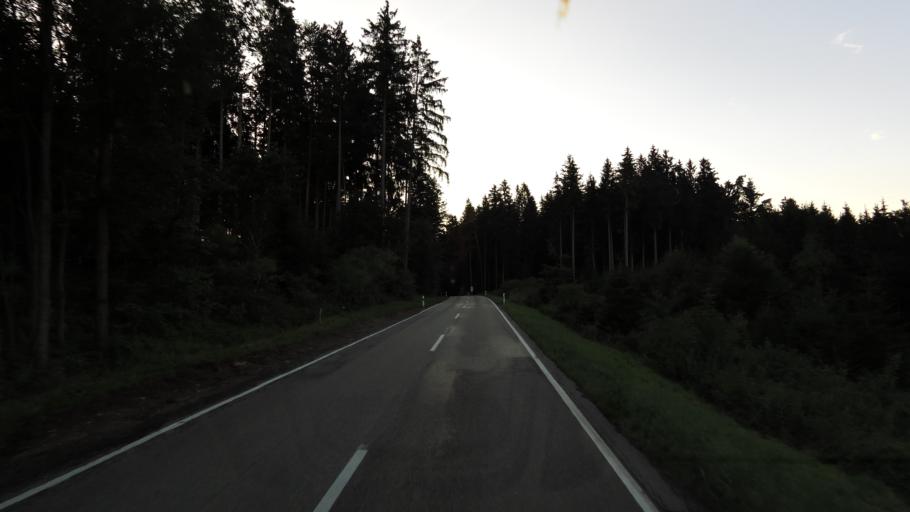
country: DE
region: Bavaria
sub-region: Upper Bavaria
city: Trostberg an der Alz
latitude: 48.0414
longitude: 12.5174
